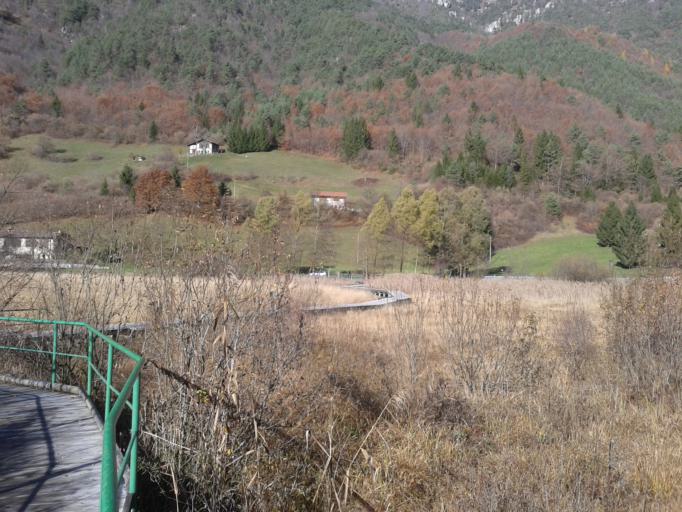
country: IT
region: Trentino-Alto Adige
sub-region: Provincia di Trento
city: Cimego
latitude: 45.8722
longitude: 10.6553
